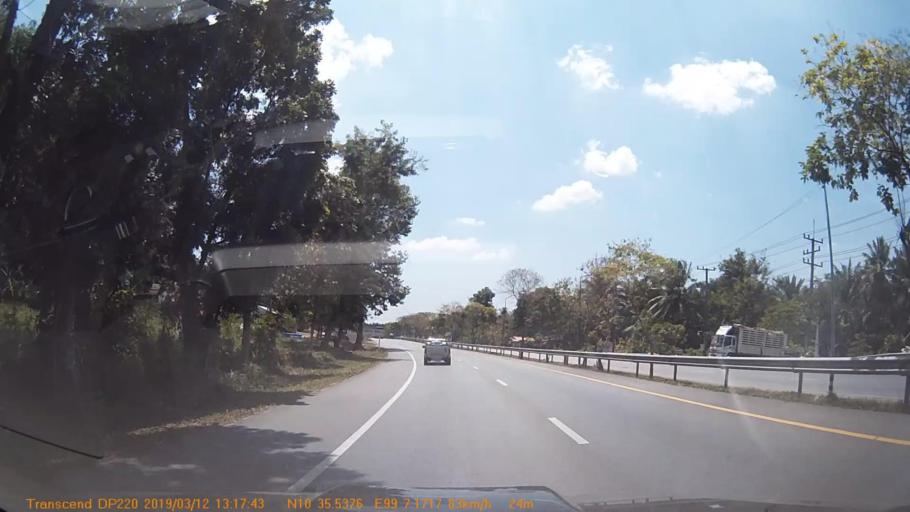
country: TH
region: Chumphon
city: Tha Sae
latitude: 10.5920
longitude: 99.1192
